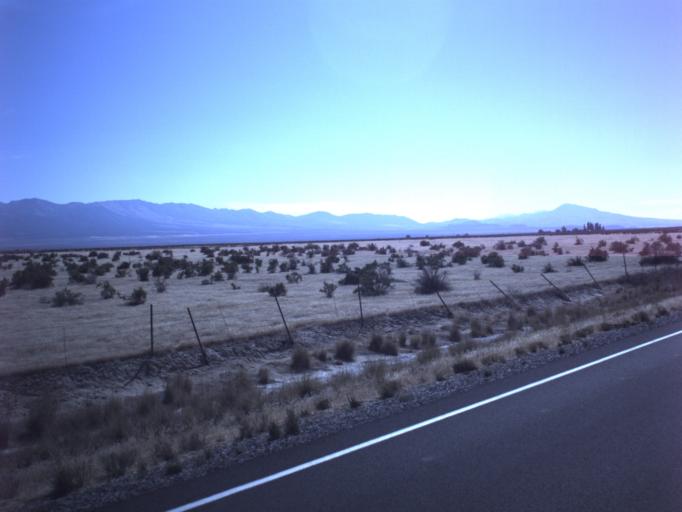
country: US
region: Utah
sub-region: Tooele County
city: Grantsville
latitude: 40.3208
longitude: -112.7439
